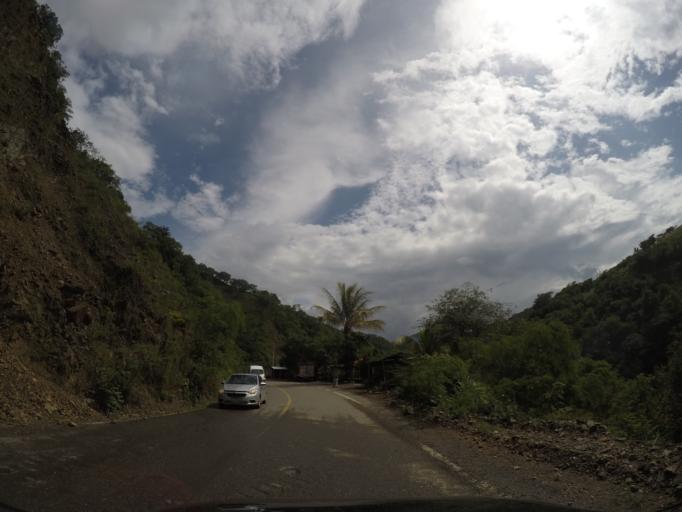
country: MX
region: Oaxaca
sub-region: San Jeronimo Coatlan
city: San Cristobal Honduras
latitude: 16.3792
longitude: -97.0765
